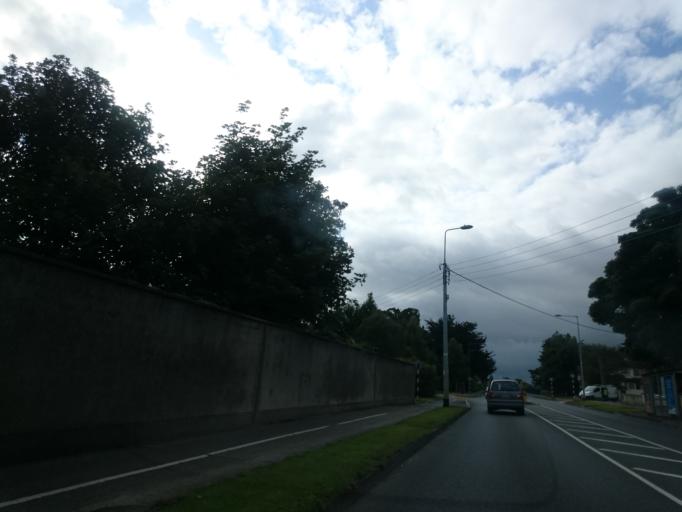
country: IE
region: Leinster
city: Mount Merrion
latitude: 53.2911
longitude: -6.2280
